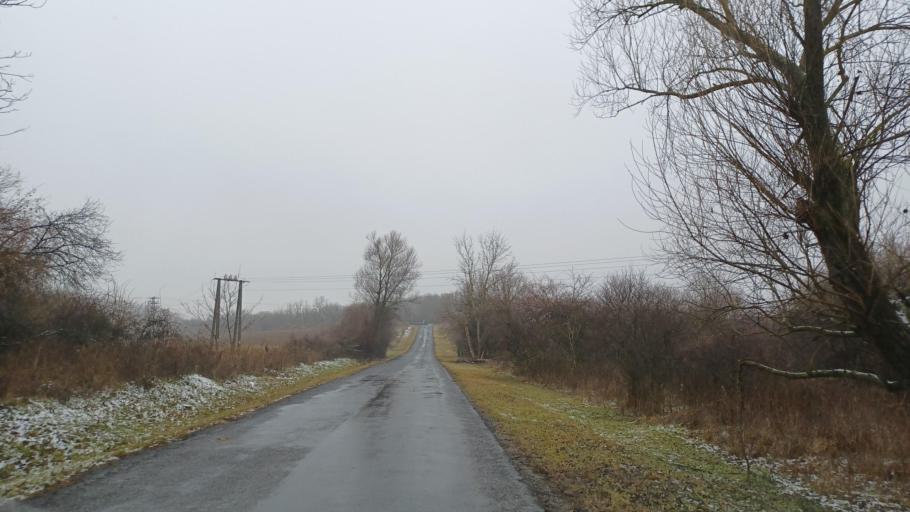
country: HU
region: Tolna
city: Gyonk
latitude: 46.6002
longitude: 18.4849
